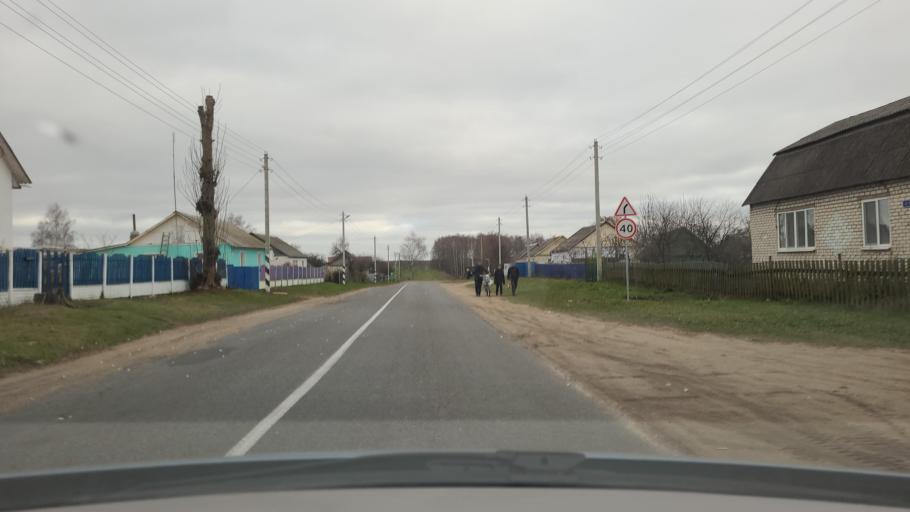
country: BY
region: Minsk
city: Khalopyenichy
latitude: 54.4697
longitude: 28.9816
